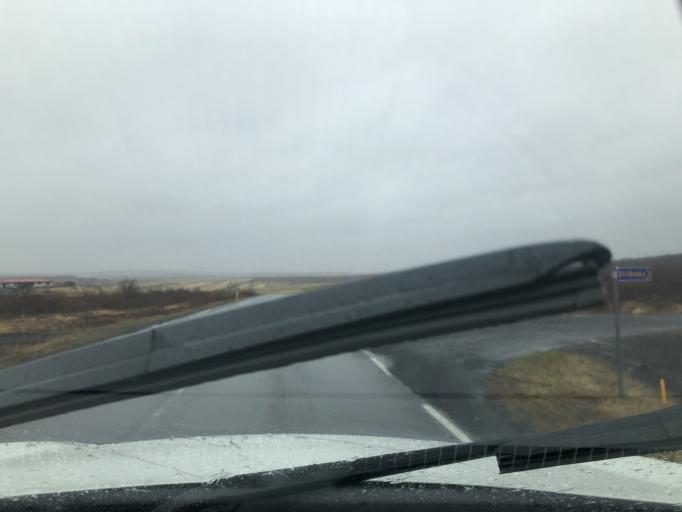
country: IS
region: South
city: Selfoss
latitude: 64.2607
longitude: -20.4724
